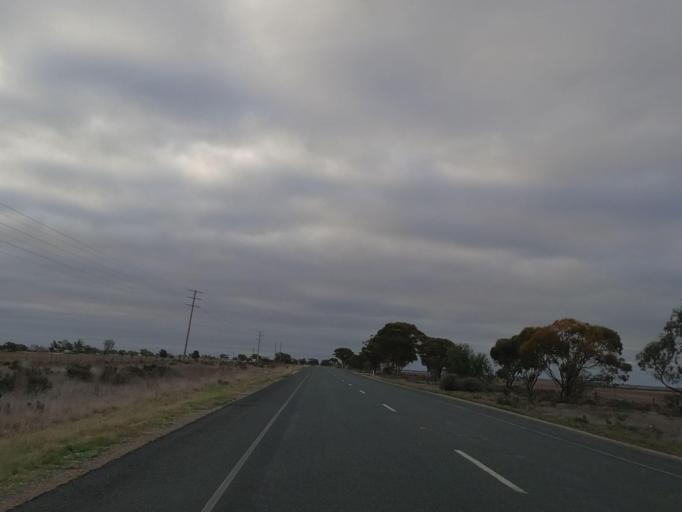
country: AU
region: Victoria
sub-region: Swan Hill
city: Swan Hill
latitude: -35.5880
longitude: 143.7904
